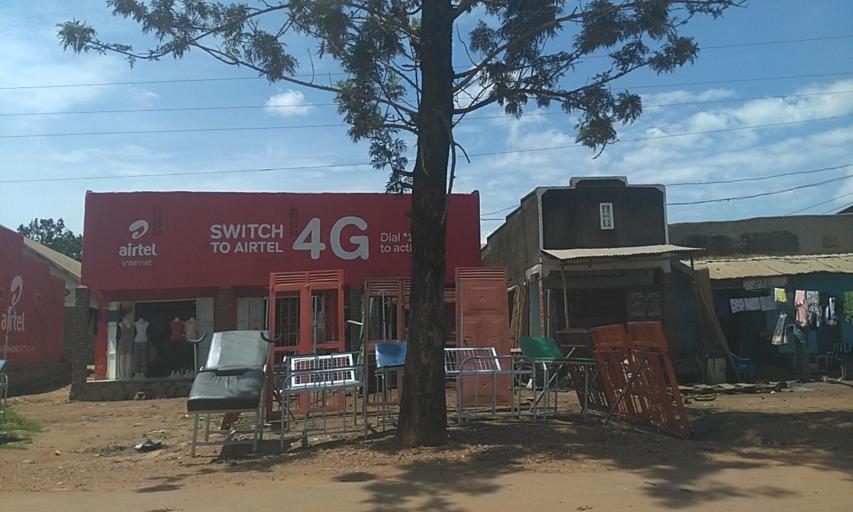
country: UG
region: Central Region
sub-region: Wakiso District
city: Wakiso
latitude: 0.3811
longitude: 32.5189
